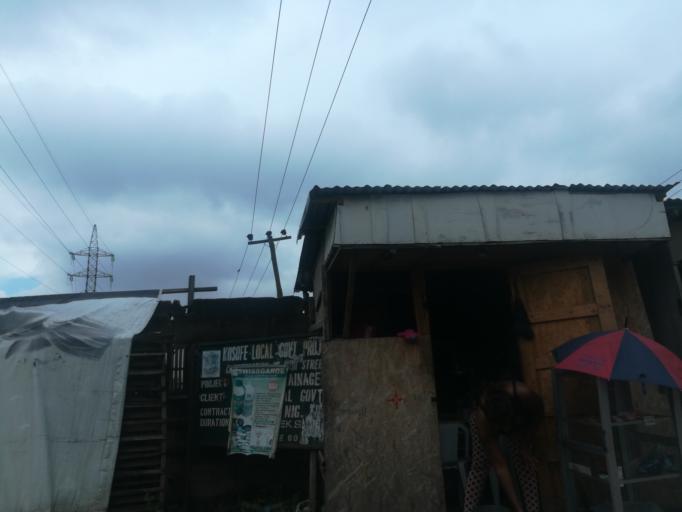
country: NG
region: Lagos
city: Ojota
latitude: 6.5758
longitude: 3.3745
